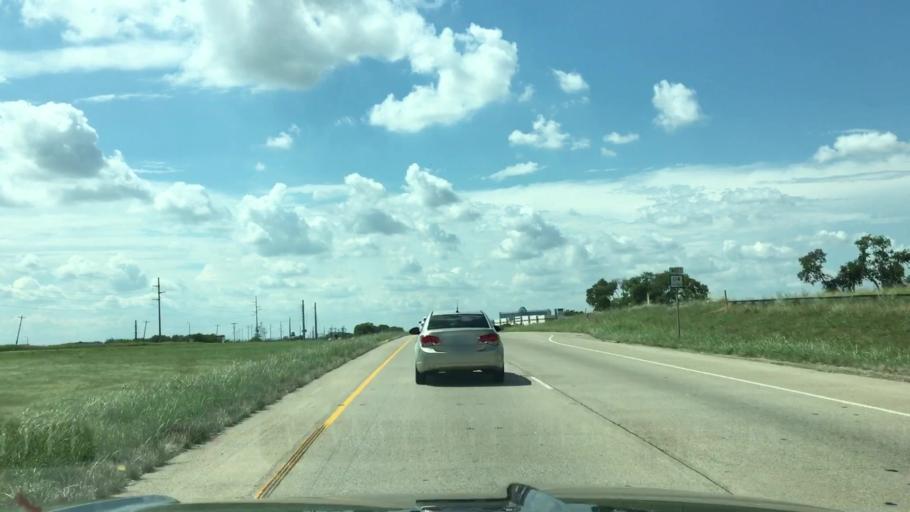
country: US
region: Texas
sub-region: Denton County
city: Roanoke
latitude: 33.0247
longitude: -97.2587
